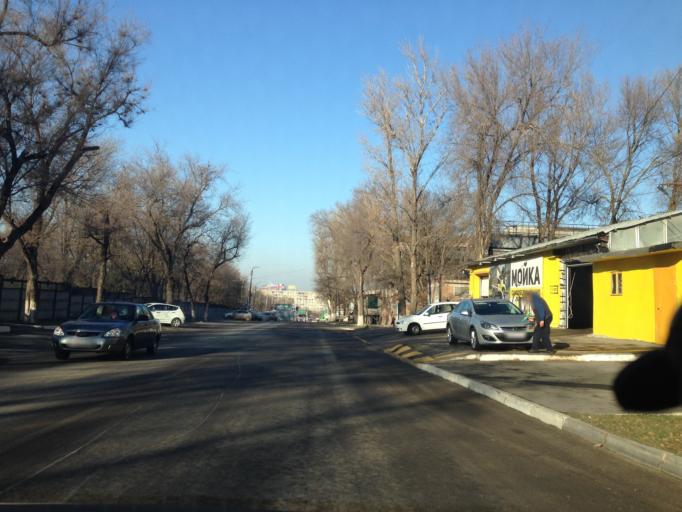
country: RU
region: Rostov
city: Rostov-na-Donu
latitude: 47.2396
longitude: 39.7189
